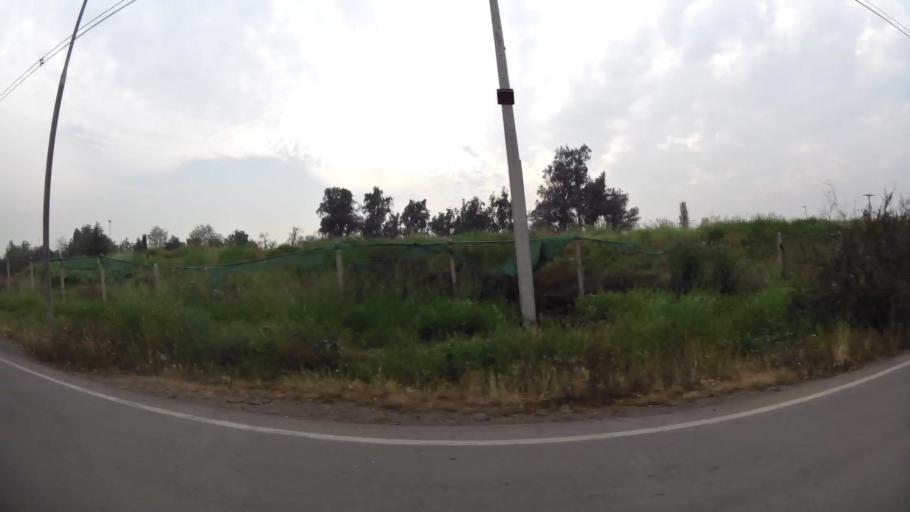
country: CL
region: Santiago Metropolitan
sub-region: Provincia de Chacabuco
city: Chicureo Abajo
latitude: -33.2162
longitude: -70.6749
